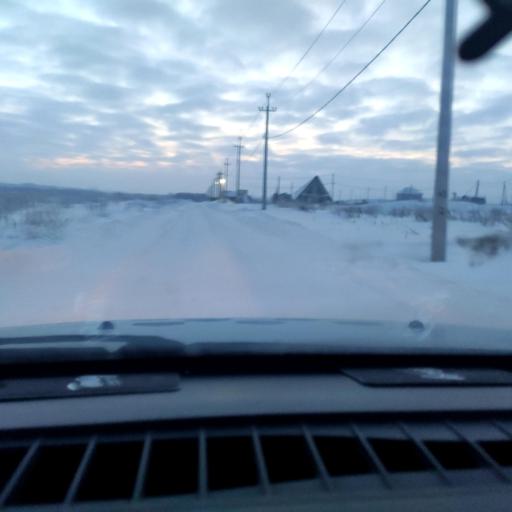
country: RU
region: Perm
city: Kultayevo
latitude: 57.8751
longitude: 55.9703
